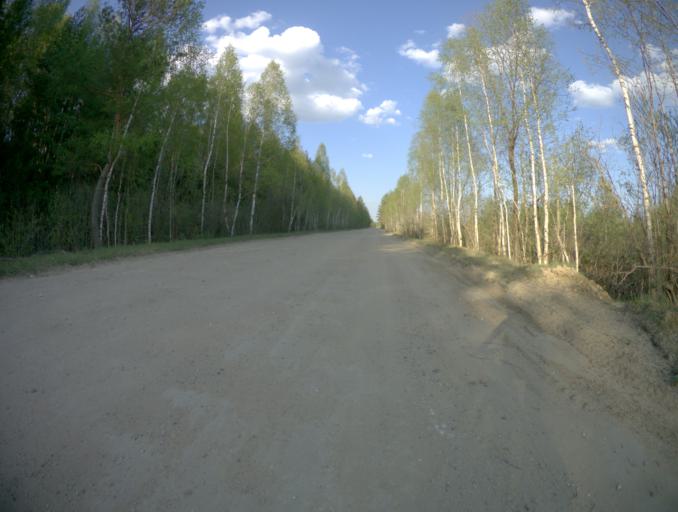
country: RU
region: Vladimir
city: Mstera
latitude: 56.5511
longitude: 41.8048
